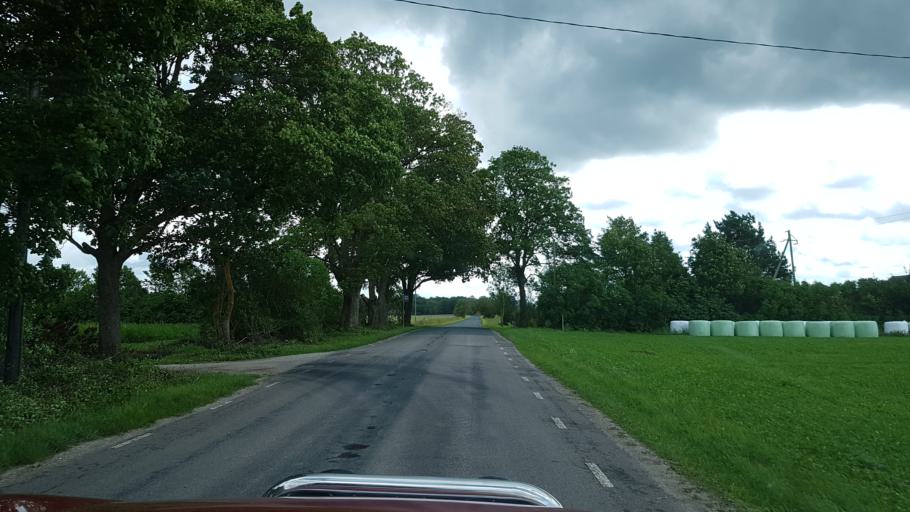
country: EE
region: Laeaene
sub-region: Lihula vald
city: Lihula
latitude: 58.7114
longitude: 24.0098
